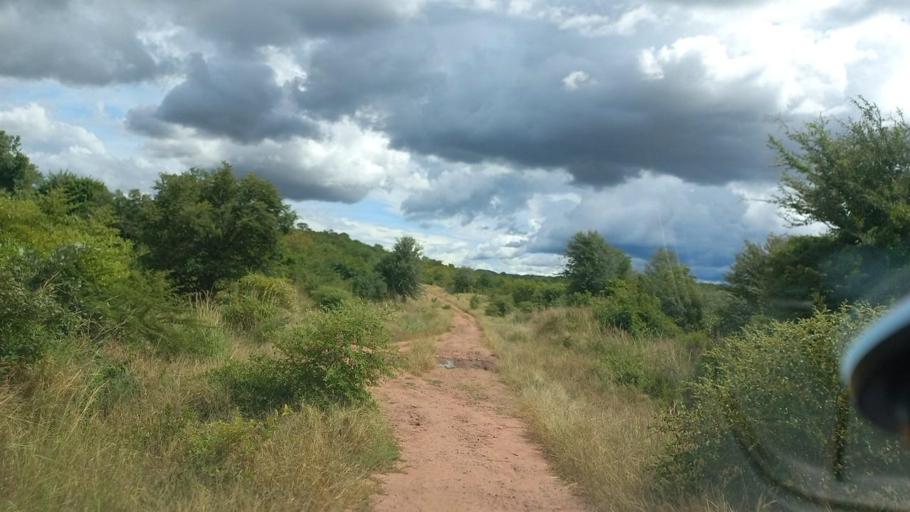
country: ZM
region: Lusaka
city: Luangwa
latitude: -15.6302
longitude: 30.3880
